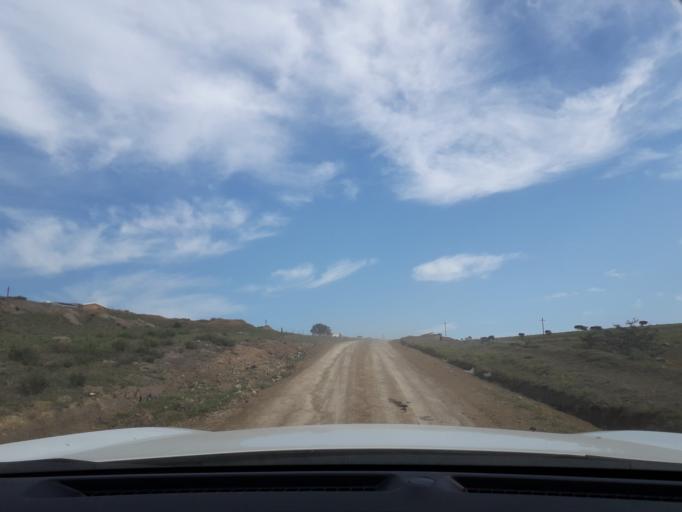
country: ZA
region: Eastern Cape
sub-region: Buffalo City Metropolitan Municipality
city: Bhisho
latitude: -32.9974
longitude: 27.3344
